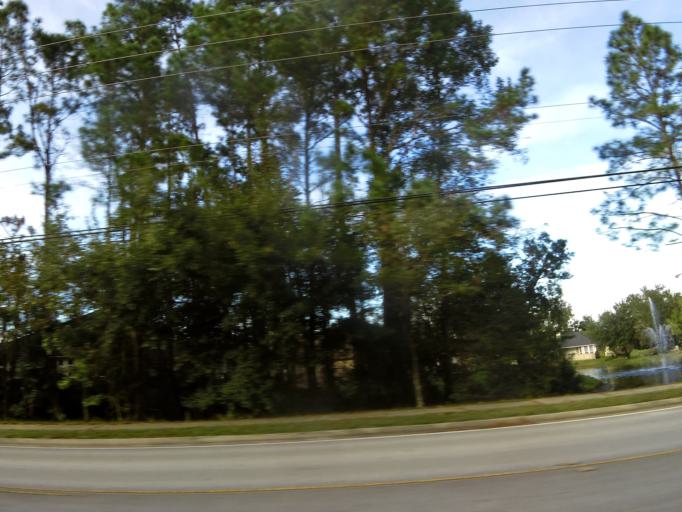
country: US
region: Florida
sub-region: Saint Johns County
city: Fruit Cove
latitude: 30.1616
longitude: -81.5698
